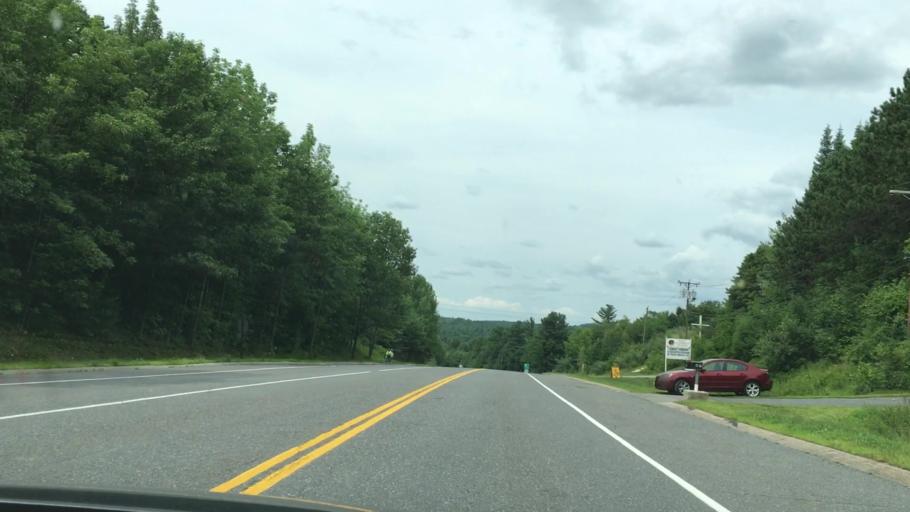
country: US
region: Massachusetts
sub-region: Worcester County
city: Gardner
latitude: 42.5988
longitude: -71.9883
